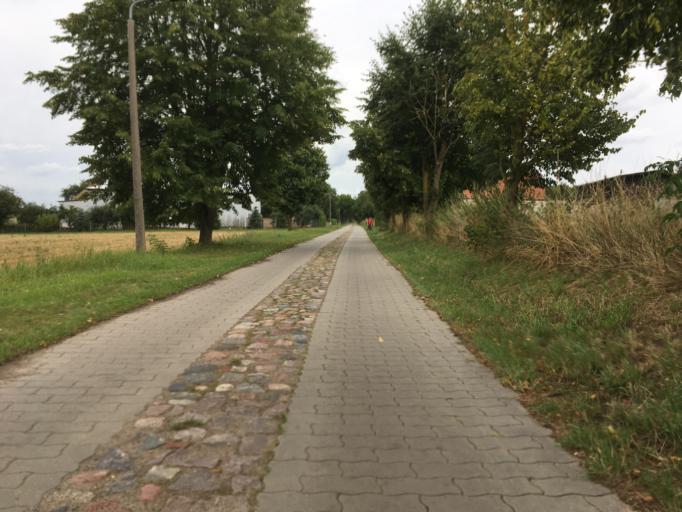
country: DE
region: Brandenburg
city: Passow
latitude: 53.1713
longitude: 14.0916
